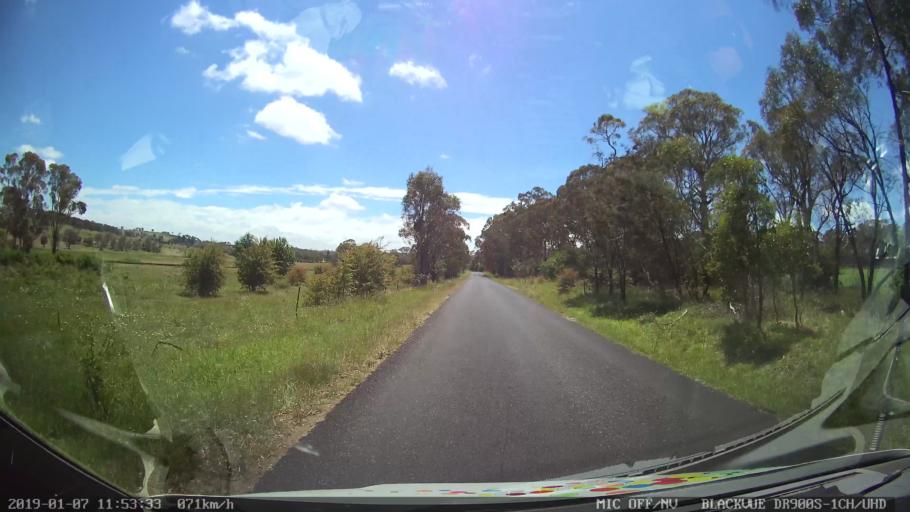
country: AU
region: New South Wales
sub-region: Guyra
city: Guyra
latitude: -30.3035
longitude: 151.6583
